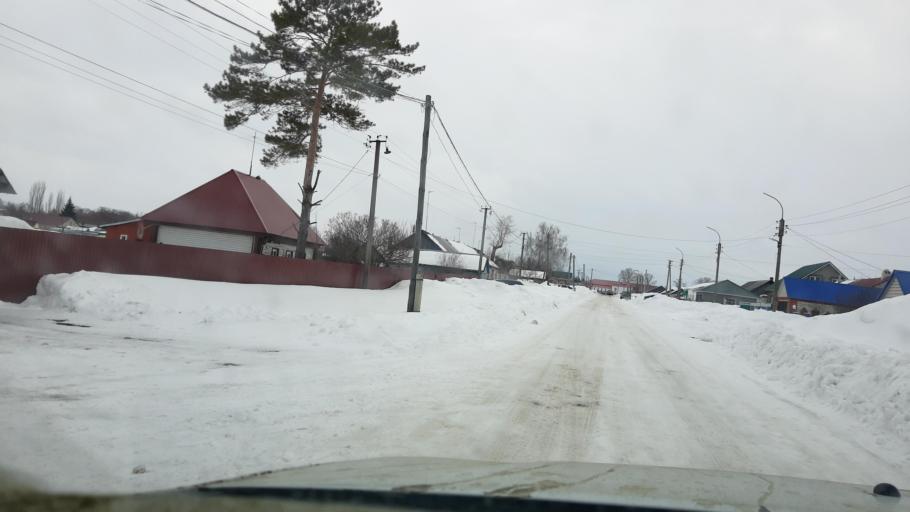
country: RU
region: Bashkortostan
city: Karmaskaly
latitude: 54.4158
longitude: 56.1622
